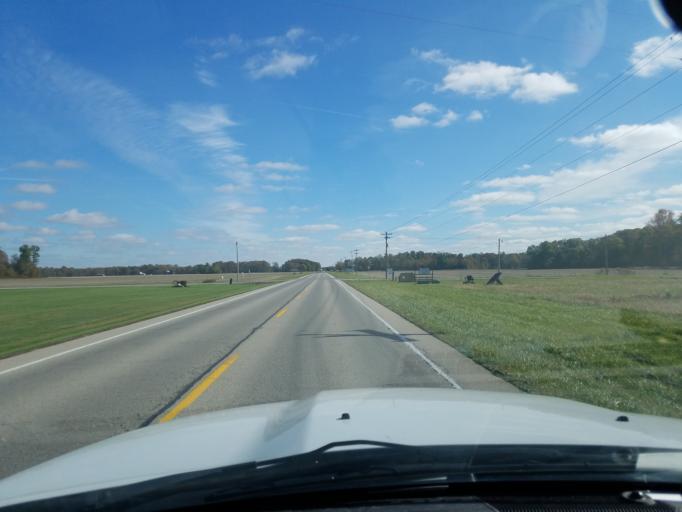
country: US
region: Indiana
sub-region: Ripley County
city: Versailles
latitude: 39.0747
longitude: -85.2938
